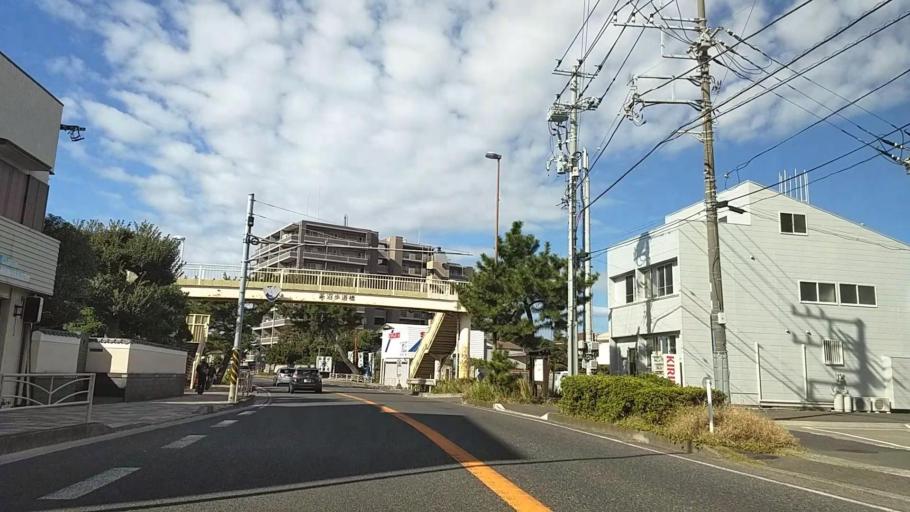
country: JP
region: Kanagawa
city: Chigasaki
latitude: 35.3376
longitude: 139.4255
